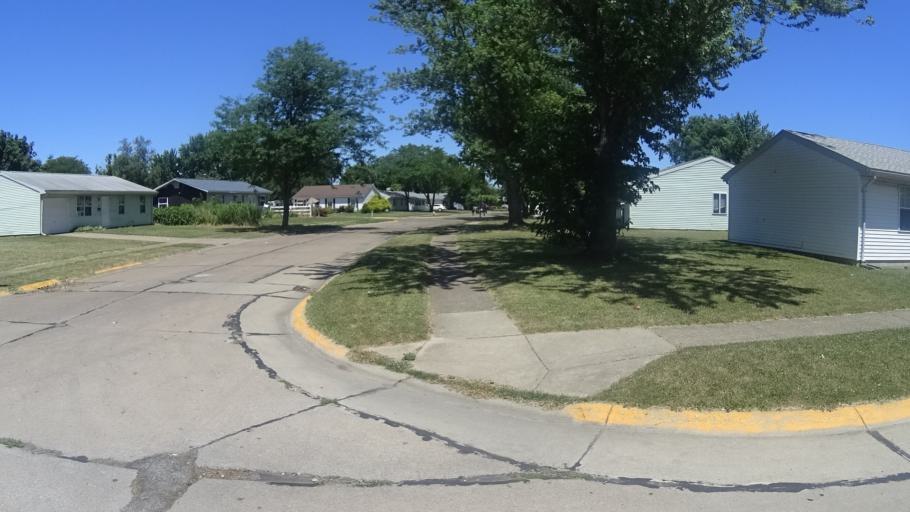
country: US
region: Ohio
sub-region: Erie County
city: Sandusky
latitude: 41.4383
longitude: -82.6867
